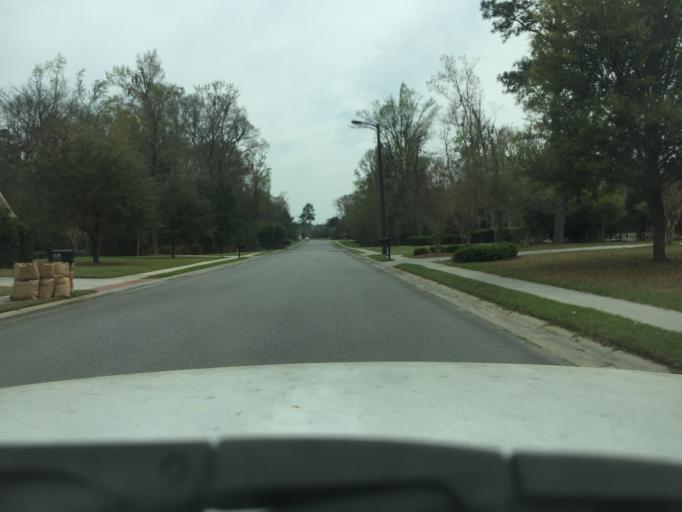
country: US
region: Georgia
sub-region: Chatham County
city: Pooler
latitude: 32.0618
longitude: -81.2433
